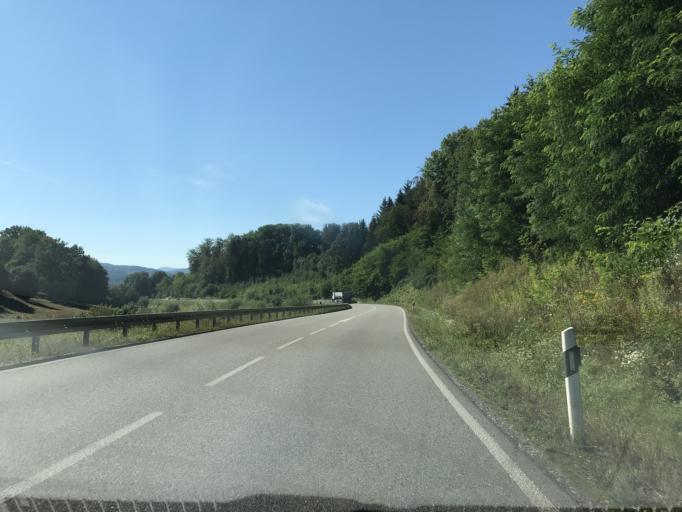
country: DE
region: Baden-Wuerttemberg
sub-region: Freiburg Region
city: Rheinfelden (Baden)
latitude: 47.5826
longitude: 7.7913
